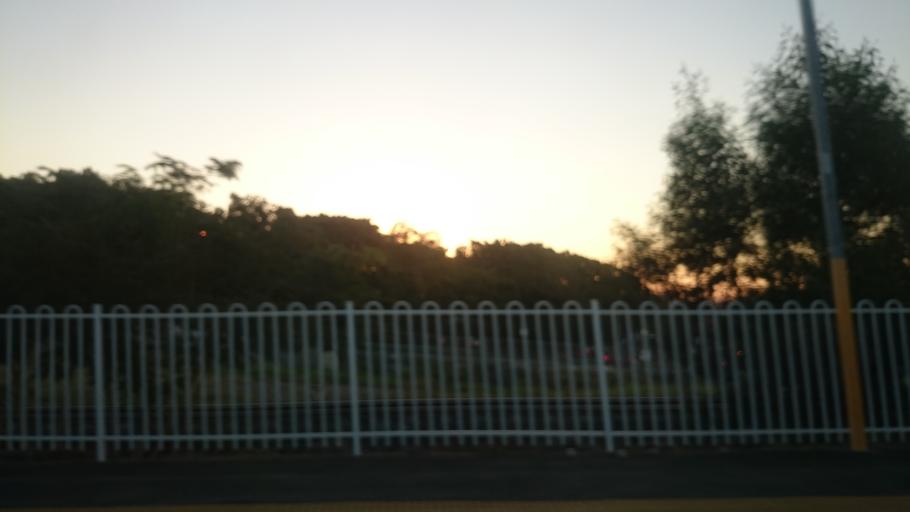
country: AU
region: Queensland
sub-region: Brisbane
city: Morningside
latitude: -27.4712
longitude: 153.0693
